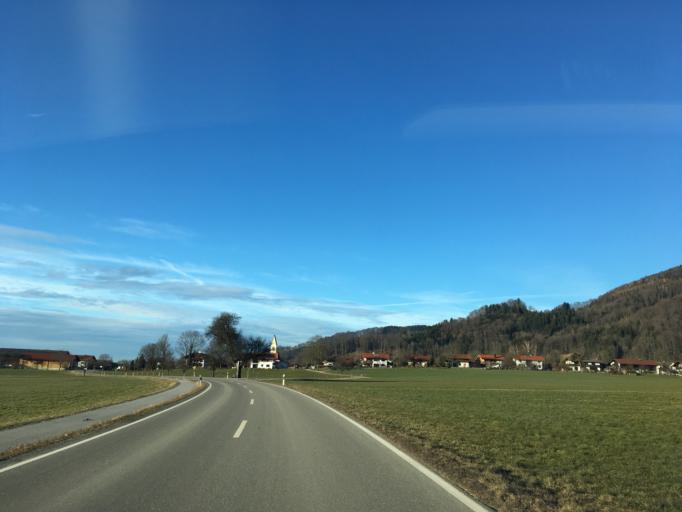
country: DE
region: Bavaria
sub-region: Upper Bavaria
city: Nussdorf am Inn
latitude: 47.7356
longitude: 12.1601
